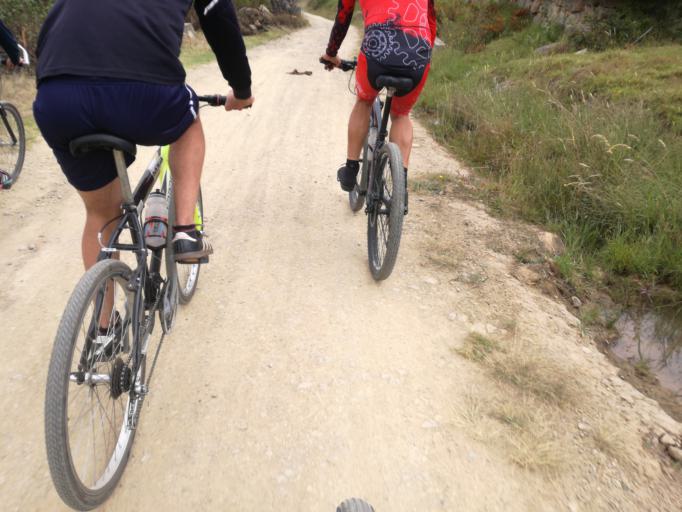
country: CO
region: Boyaca
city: Socha Viejo
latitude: 6.0069
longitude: -72.6860
